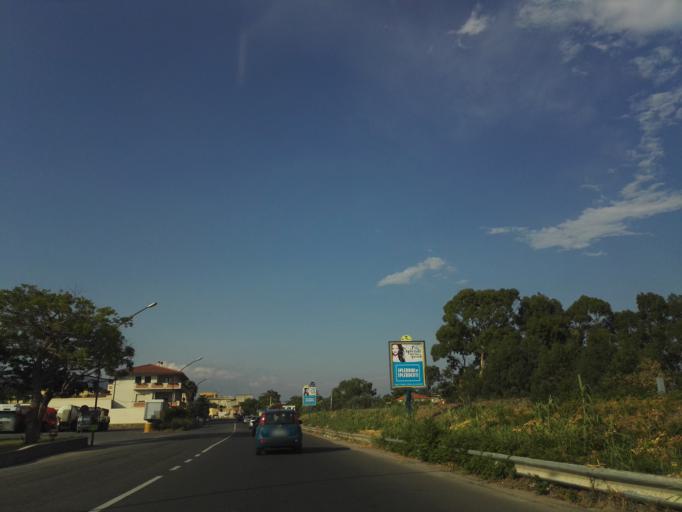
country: IT
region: Calabria
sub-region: Provincia di Reggio Calabria
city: Siderno
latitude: 38.2761
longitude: 16.3069
